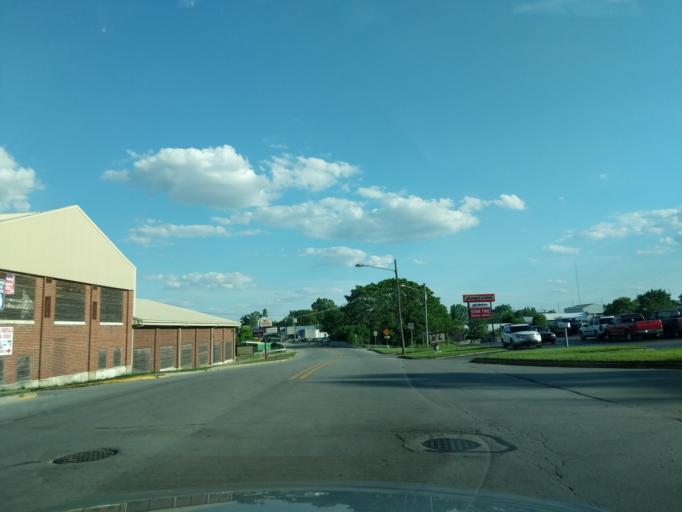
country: US
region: Indiana
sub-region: Whitley County
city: Columbia City
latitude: 41.1538
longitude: -85.4884
